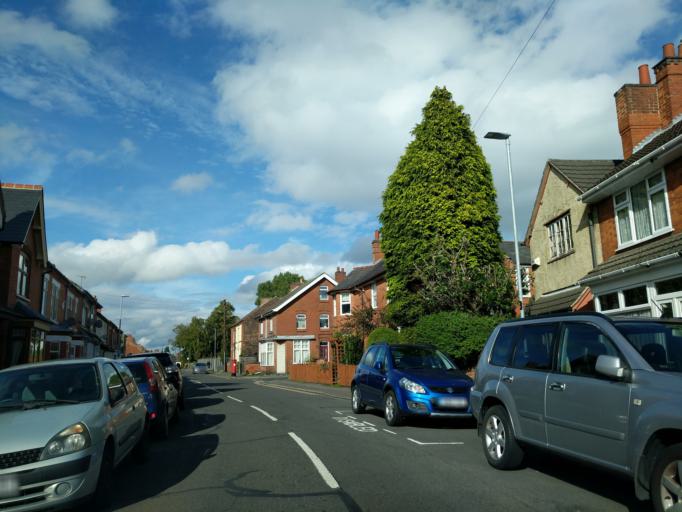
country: GB
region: England
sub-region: Leicestershire
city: Coalville
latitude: 52.7165
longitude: -1.3770
